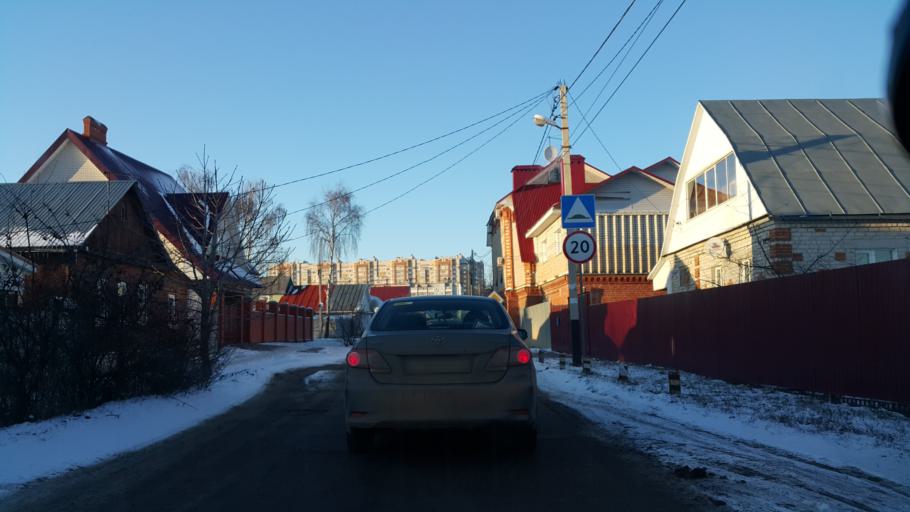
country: RU
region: Tambov
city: Pokrovo-Prigorodnoye
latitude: 52.7011
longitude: 41.4020
